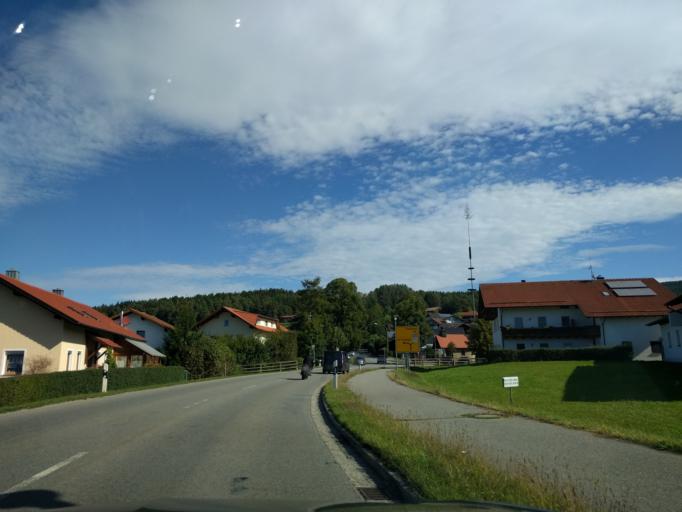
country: DE
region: Bavaria
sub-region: Upper Palatinate
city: Kotzting
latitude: 49.1799
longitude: 12.8700
